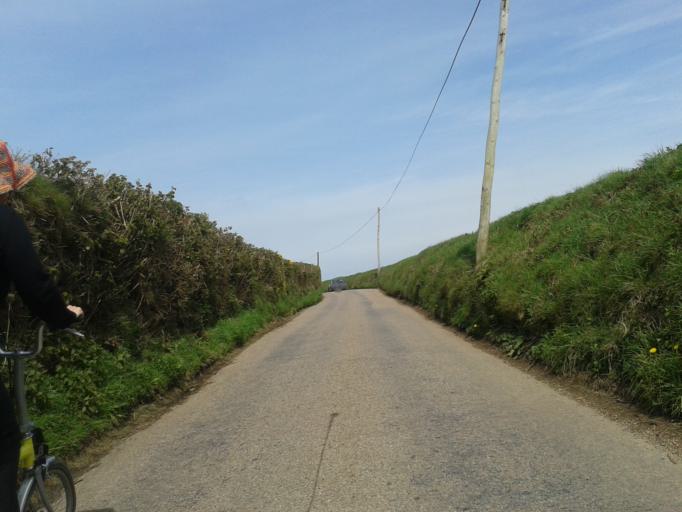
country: GB
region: England
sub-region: Devon
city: Braunton
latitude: 51.1535
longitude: -4.1913
